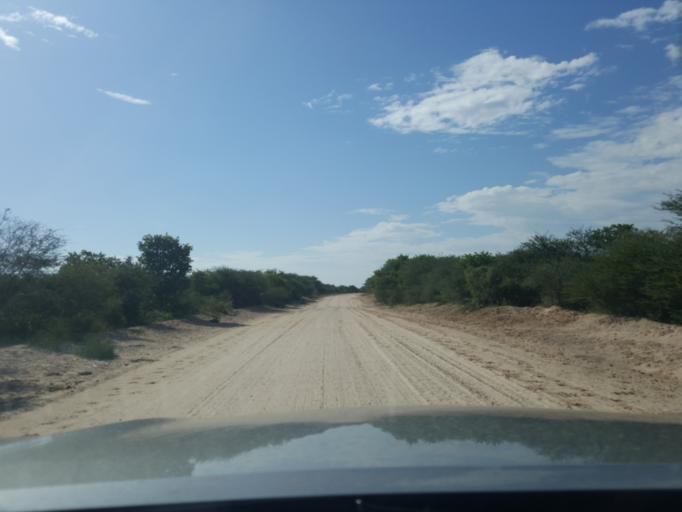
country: BW
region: Kweneng
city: Khudumelapye
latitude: -23.4837
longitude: 24.6934
